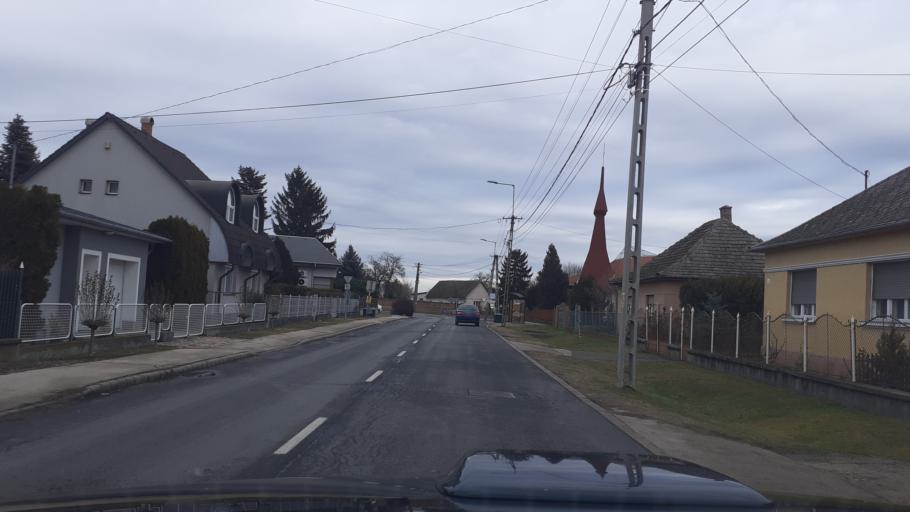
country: HU
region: Fejer
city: dunaujvaros
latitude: 46.9783
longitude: 18.9216
